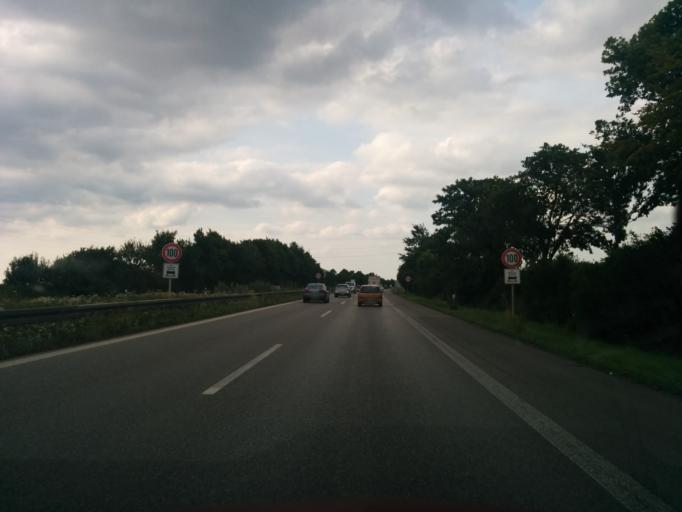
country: DE
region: Bavaria
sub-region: Swabia
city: Konigsbrunn
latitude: 48.2597
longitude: 10.8666
